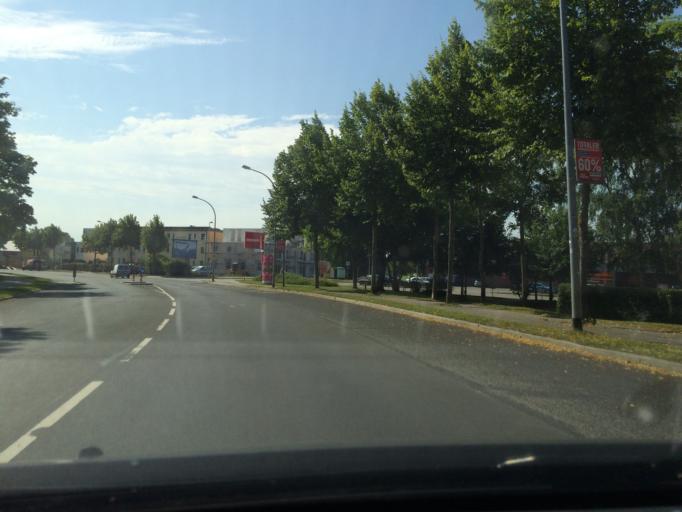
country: DE
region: Mecklenburg-Vorpommern
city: Stralsund
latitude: 54.3034
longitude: 13.0915
